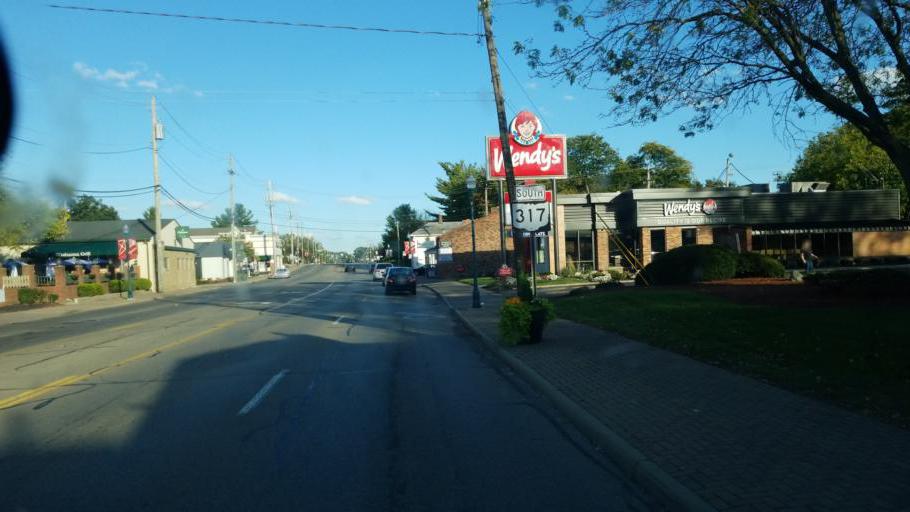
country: US
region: Ohio
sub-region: Franklin County
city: Gahanna
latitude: 40.0188
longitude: -82.8793
